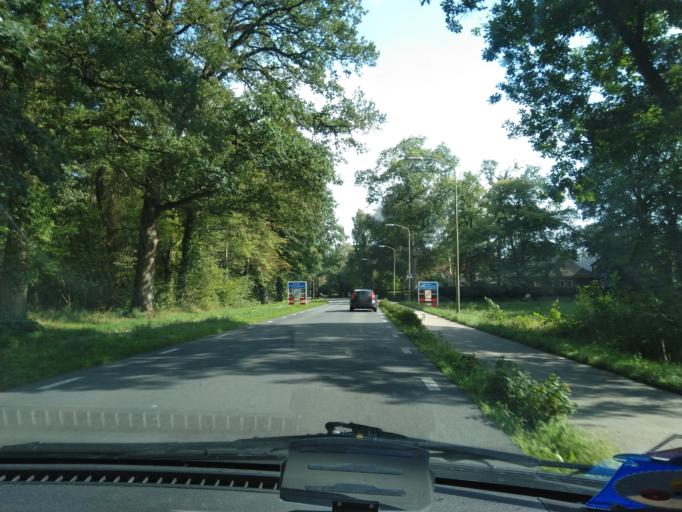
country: NL
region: Groningen
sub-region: Gemeente Haren
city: Haren
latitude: 53.1623
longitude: 6.5570
